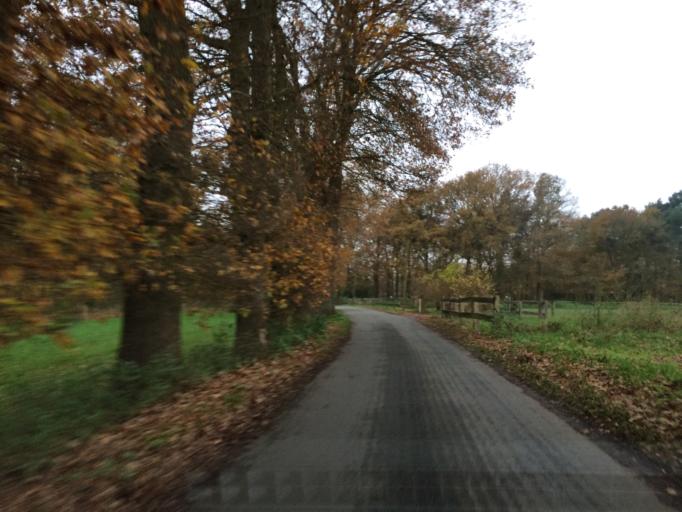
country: DE
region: North Rhine-Westphalia
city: Marl
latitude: 51.6801
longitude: 7.0575
